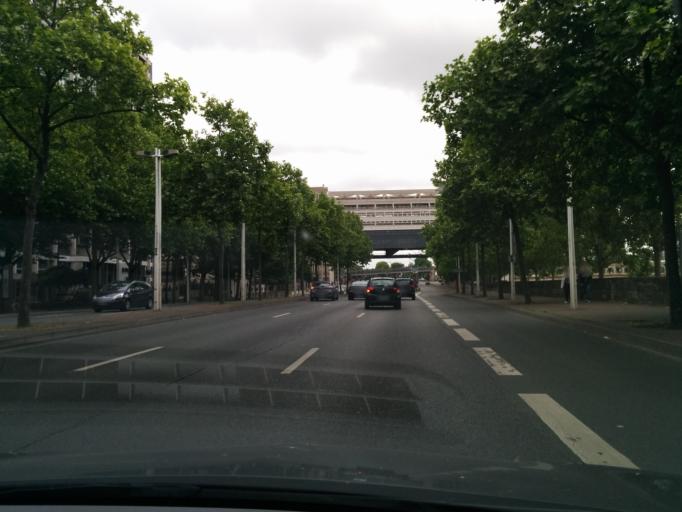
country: FR
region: Ile-de-France
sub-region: Paris
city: Paris
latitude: 48.8410
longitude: 2.3734
